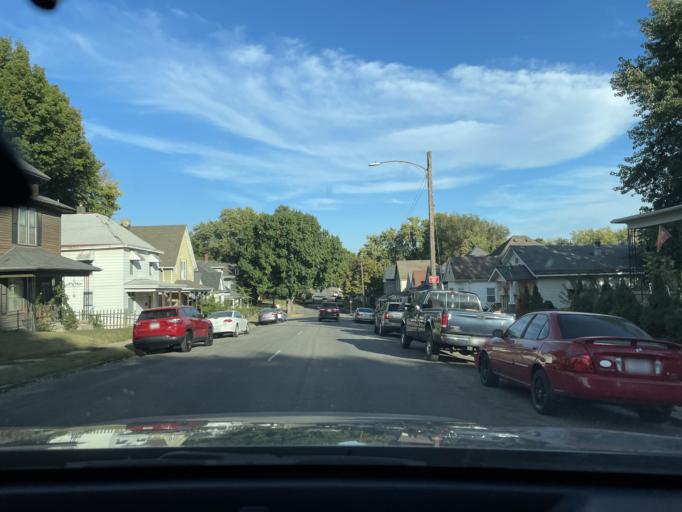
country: US
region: Missouri
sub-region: Buchanan County
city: Saint Joseph
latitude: 39.7683
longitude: -94.8331
